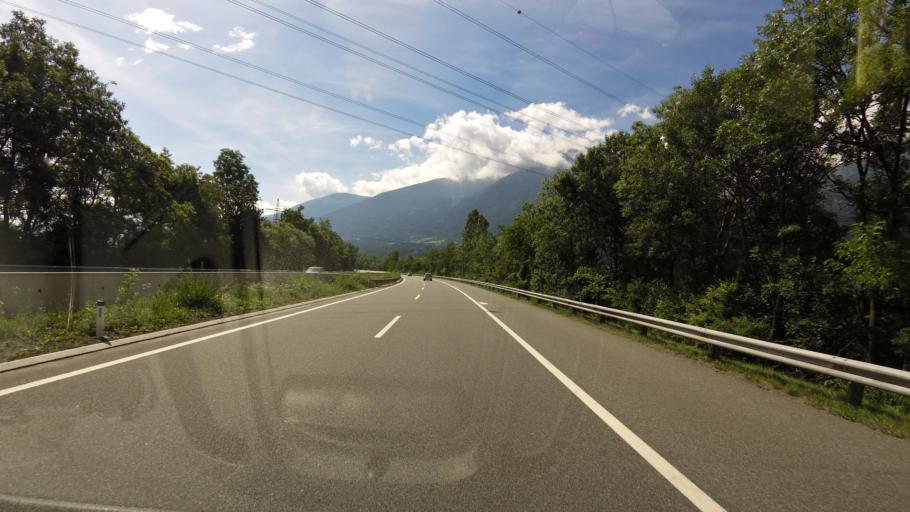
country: AT
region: Tyrol
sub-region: Politischer Bezirk Innsbruck Land
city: Pettnau
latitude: 47.3047
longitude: 11.1222
